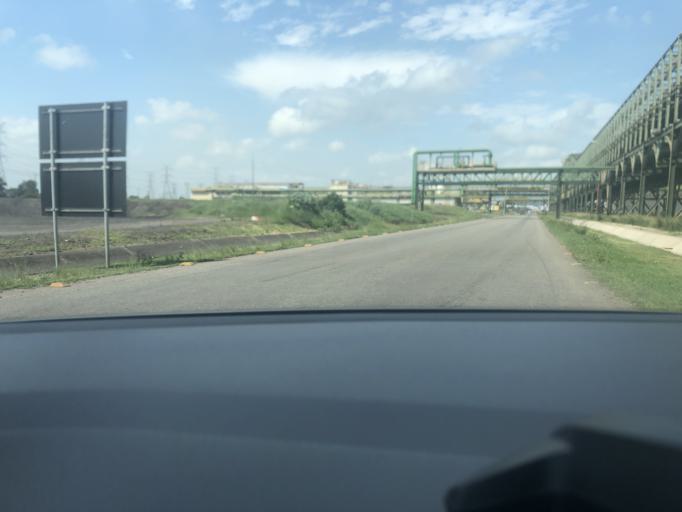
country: BR
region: Rio de Janeiro
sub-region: Itaguai
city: Itaguai
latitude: -22.9059
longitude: -43.7406
